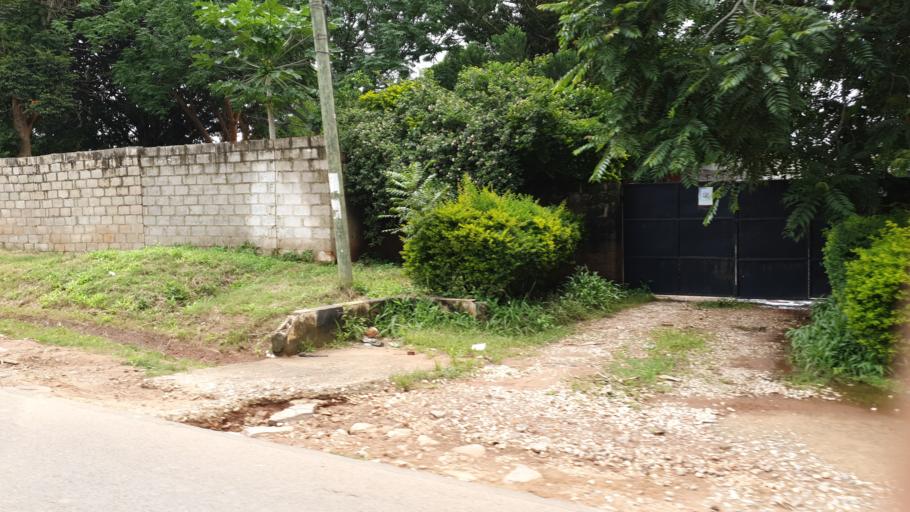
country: ZM
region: Lusaka
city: Lusaka
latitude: -15.4271
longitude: 28.3083
